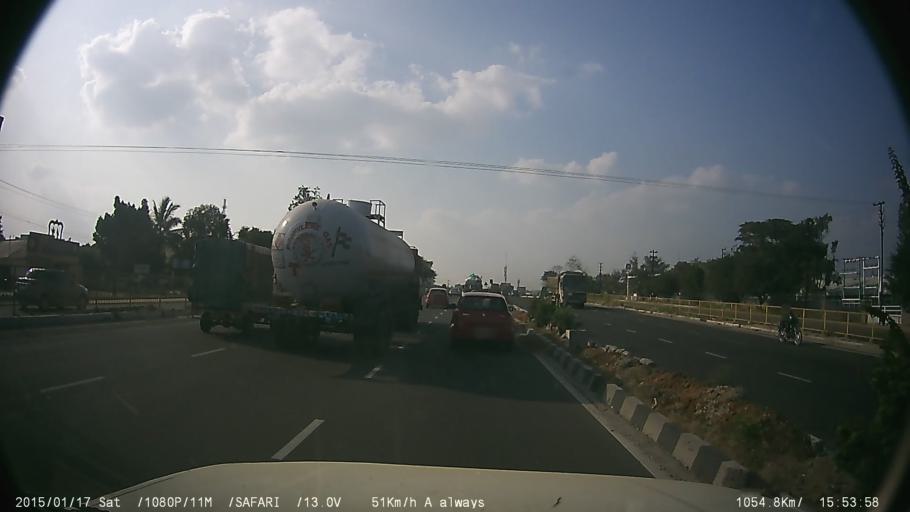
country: IN
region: Tamil Nadu
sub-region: Krishnagiri
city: Hosur
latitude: 12.7484
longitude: 77.8080
